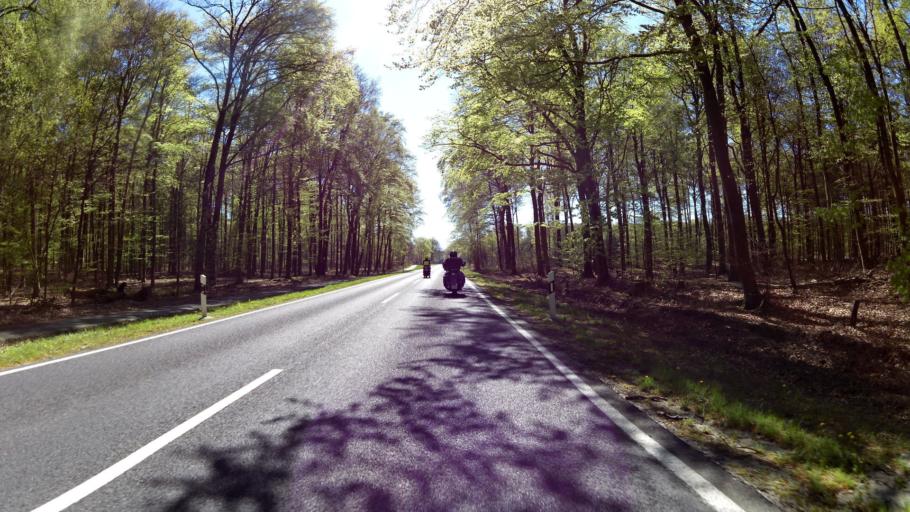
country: DE
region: Brandenburg
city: Wandlitz
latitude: 52.7195
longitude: 13.5217
